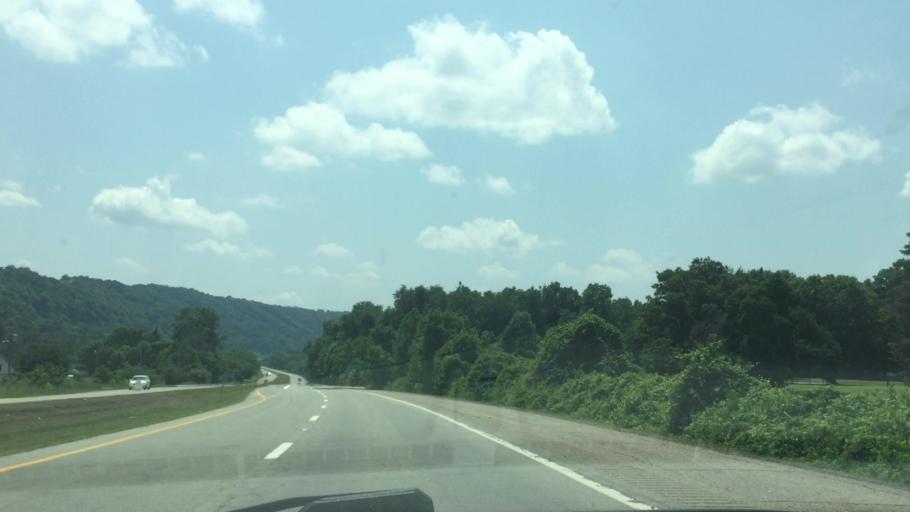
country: US
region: Ohio
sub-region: Belmont County
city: Powhatan Point
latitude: 39.8951
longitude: -80.7916
